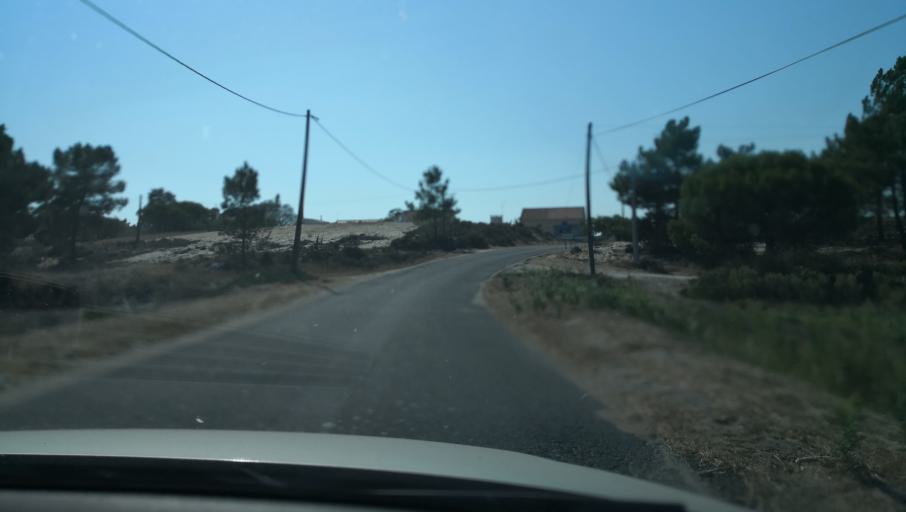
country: PT
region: Setubal
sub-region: Setubal
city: Setubal
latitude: 38.3979
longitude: -8.7691
